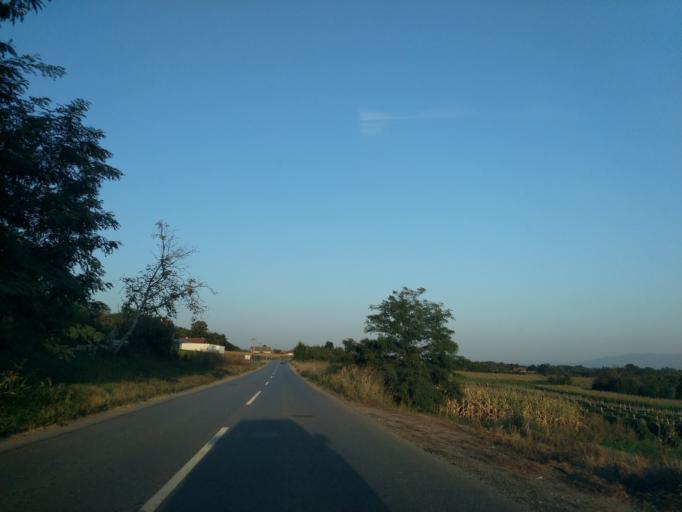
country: RS
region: Central Serbia
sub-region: Rasinski Okrug
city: Trstenik
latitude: 43.6293
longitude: 21.0468
